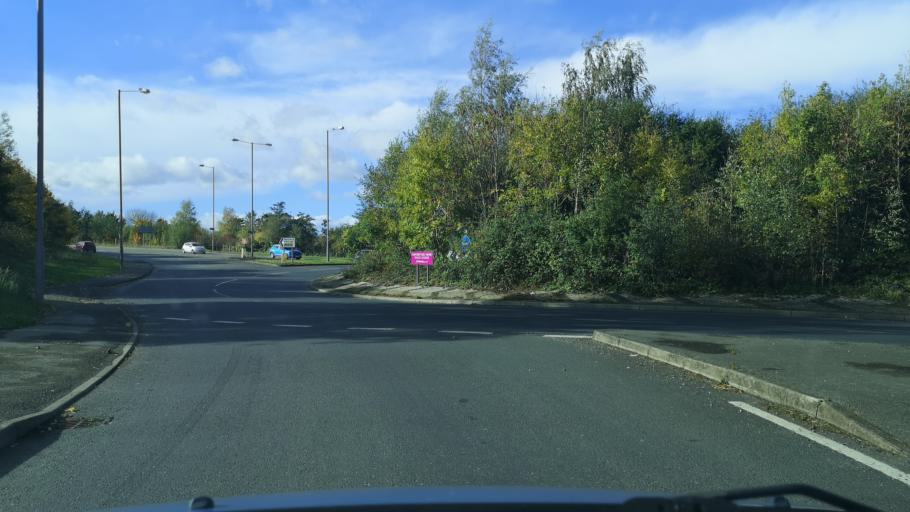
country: GB
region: England
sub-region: City and Borough of Wakefield
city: Normanton
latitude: 53.6909
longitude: -1.4010
